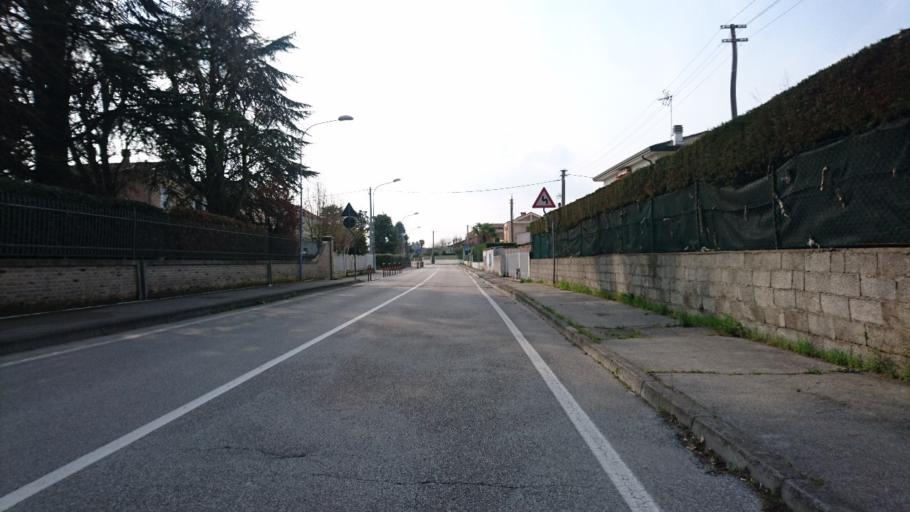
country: IT
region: Veneto
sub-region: Provincia di Padova
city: San Vito
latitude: 45.4105
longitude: 11.9712
